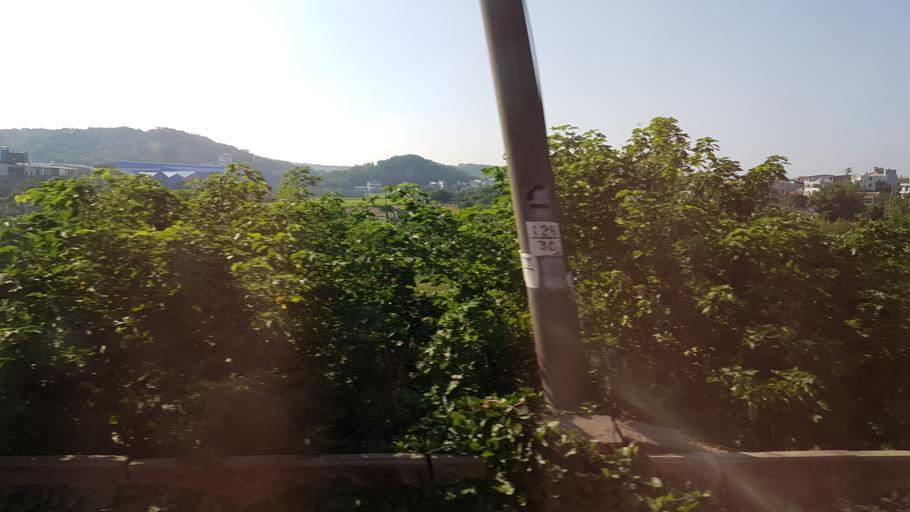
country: TW
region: Taiwan
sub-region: Miaoli
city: Miaoli
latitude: 24.6512
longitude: 120.8762
